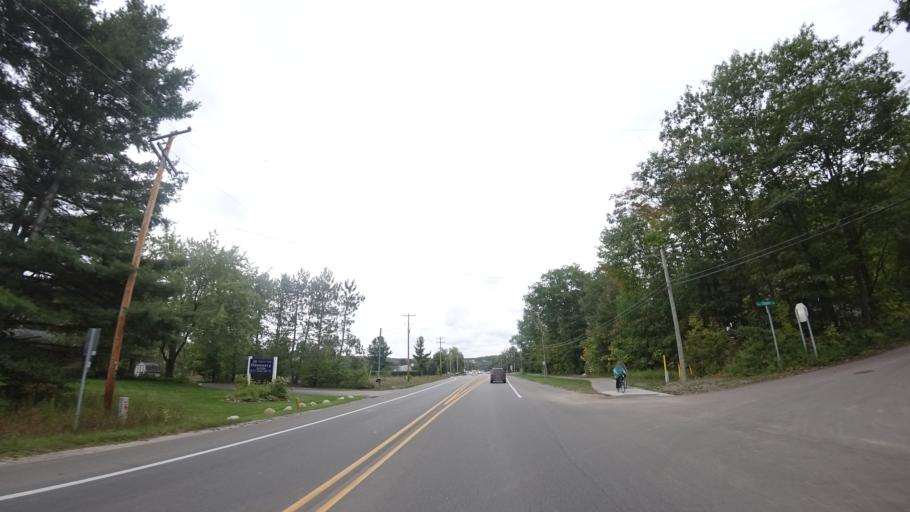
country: US
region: Michigan
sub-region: Emmet County
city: Petoskey
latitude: 45.4065
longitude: -84.9021
